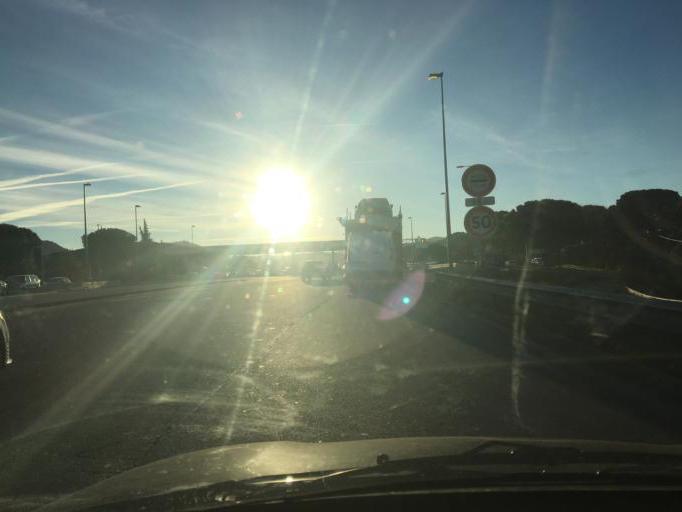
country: FR
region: Provence-Alpes-Cote d'Azur
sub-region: Departement du Var
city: Le Muy
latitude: 43.4615
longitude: 6.5496
